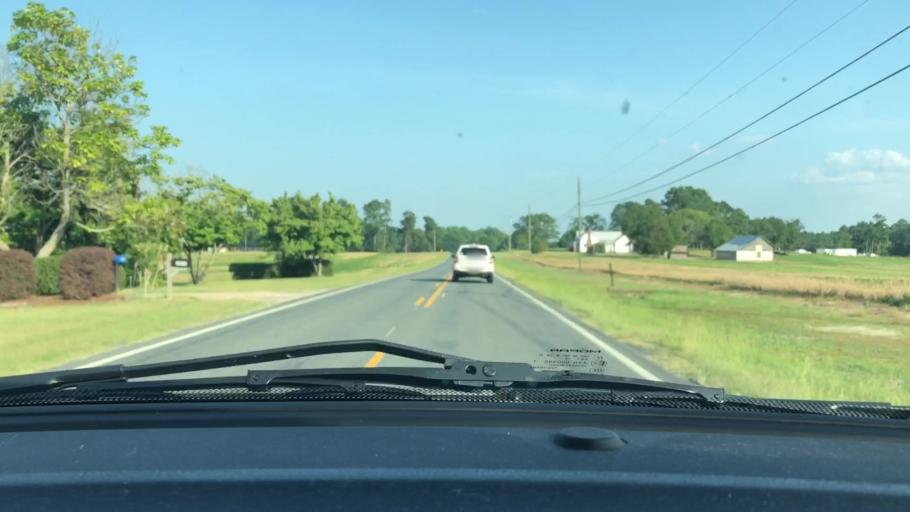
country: US
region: North Carolina
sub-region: Lee County
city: Broadway
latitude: 35.3664
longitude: -79.0940
